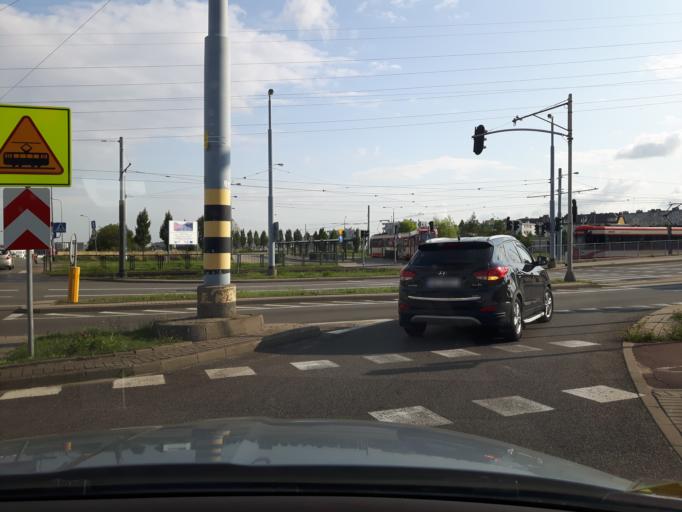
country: PL
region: Pomeranian Voivodeship
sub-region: Gdansk
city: Gdansk
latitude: 54.3384
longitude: 18.6181
